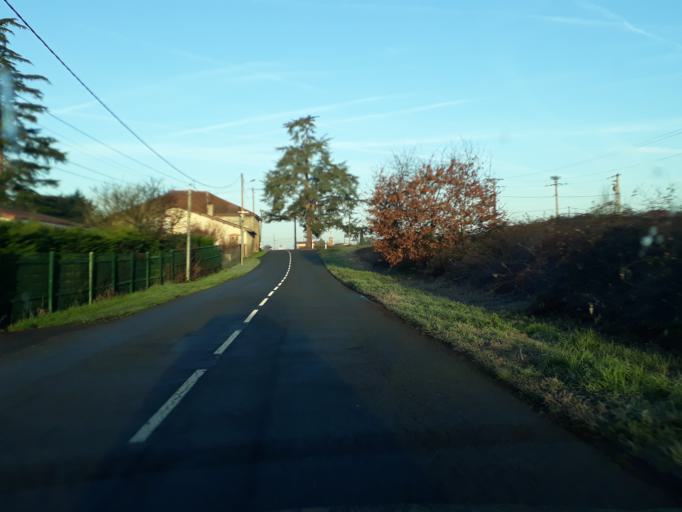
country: FR
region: Midi-Pyrenees
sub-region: Departement de la Haute-Garonne
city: Marquefave
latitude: 43.3195
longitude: 1.2350
